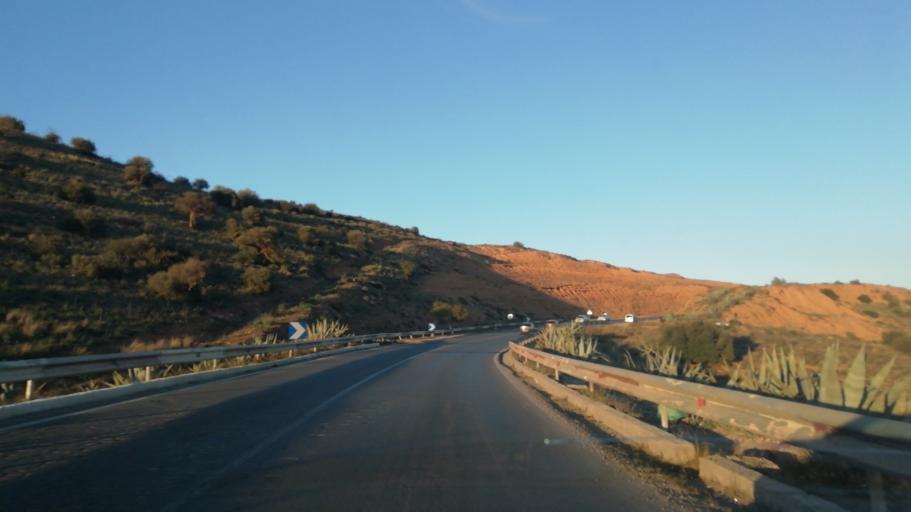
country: DZ
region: Tlemcen
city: Nedroma
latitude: 34.8900
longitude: -1.6687
